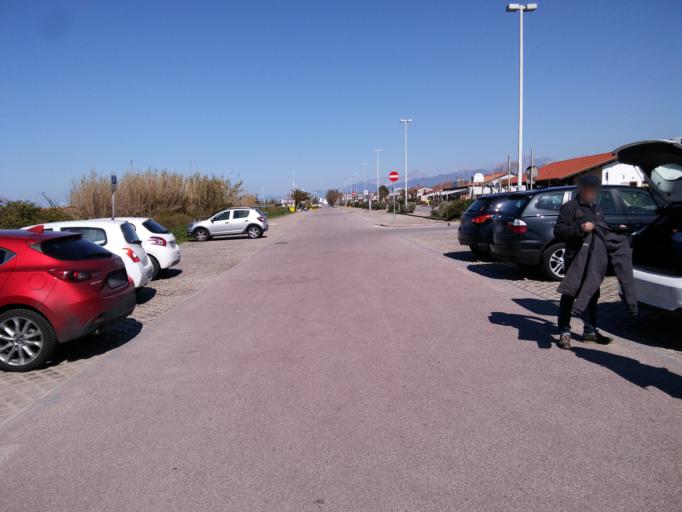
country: IT
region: Tuscany
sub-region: Provincia di Lucca
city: Viareggio
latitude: 43.8471
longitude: 10.2474
